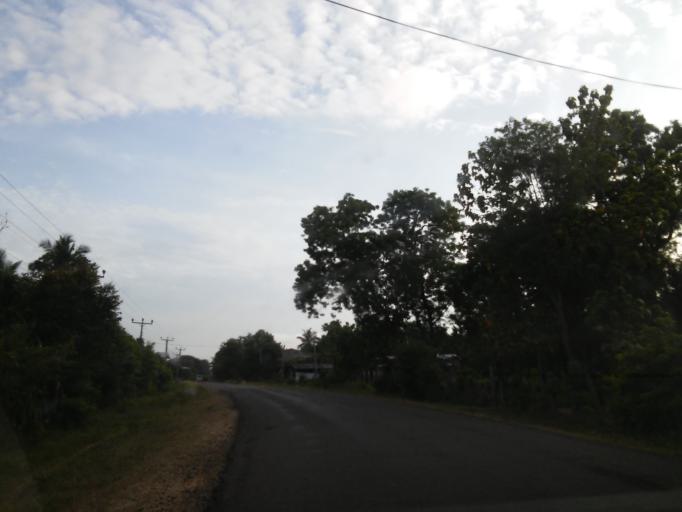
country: LK
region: Central
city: Sigiriya
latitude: 8.1195
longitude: 80.6328
